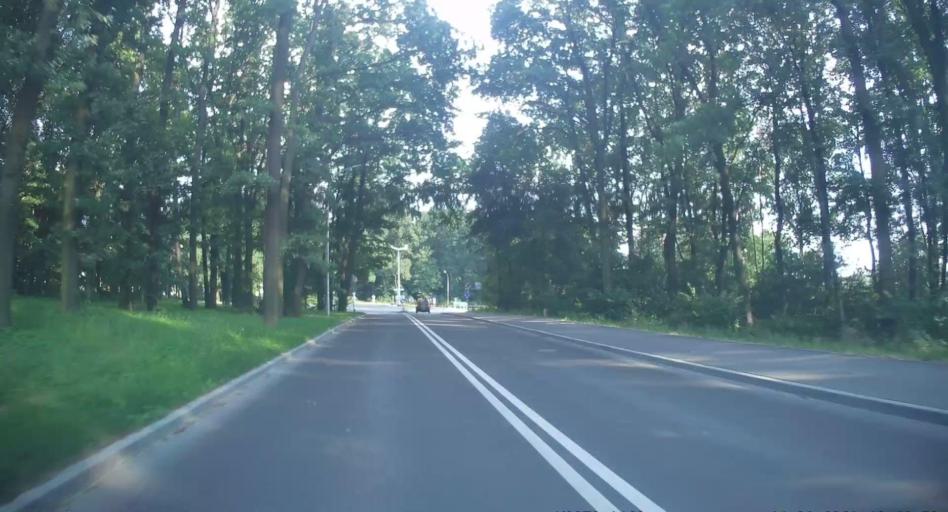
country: PL
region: Subcarpathian Voivodeship
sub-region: Powiat debicki
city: Debica
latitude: 50.0394
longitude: 21.3901
